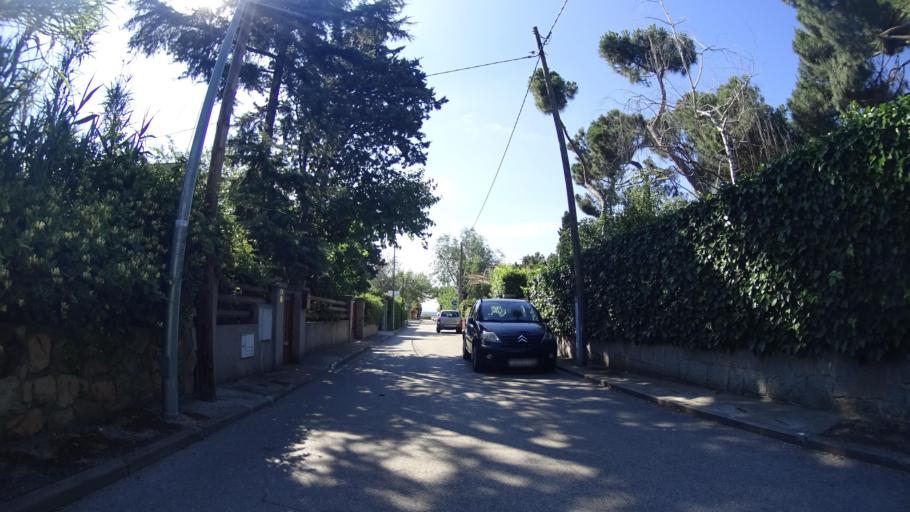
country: ES
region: Madrid
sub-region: Provincia de Madrid
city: Las Matas
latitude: 40.5490
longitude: -3.8911
